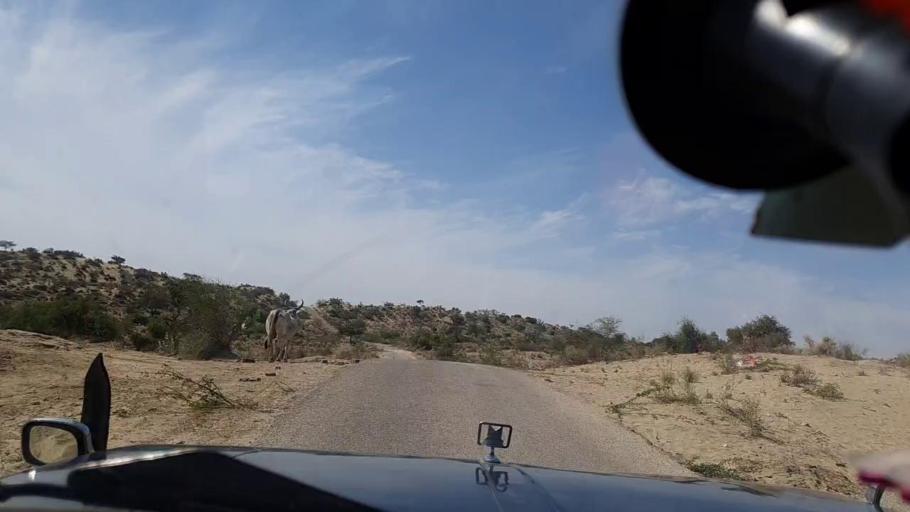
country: PK
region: Sindh
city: Diplo
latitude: 24.4105
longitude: 69.5851
